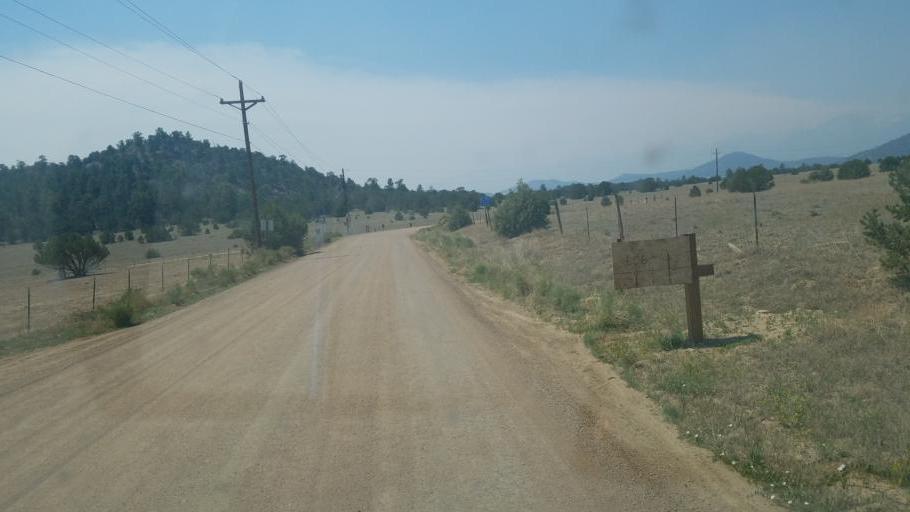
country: US
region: Colorado
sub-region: Custer County
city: Westcliffe
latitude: 38.3003
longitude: -105.4865
